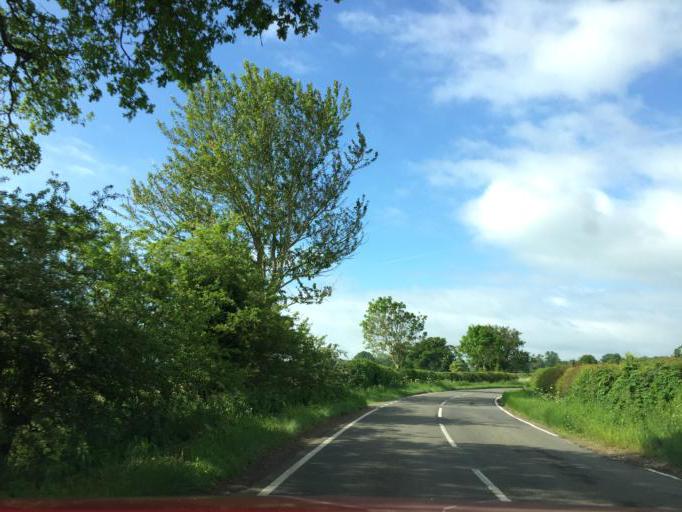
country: GB
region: England
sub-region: Northamptonshire
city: Towcester
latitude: 52.1306
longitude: -0.9580
